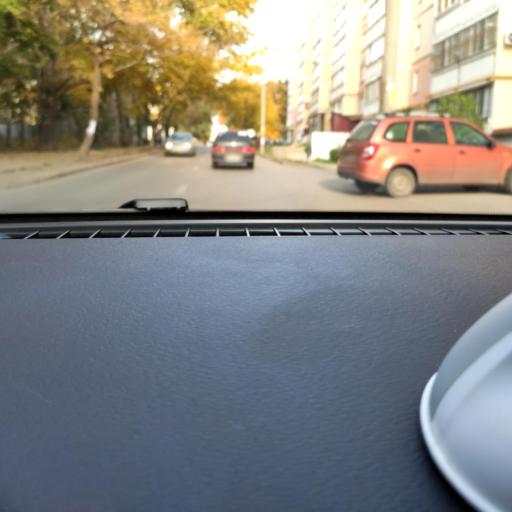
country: RU
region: Samara
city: Samara
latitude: 53.2445
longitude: 50.2463
